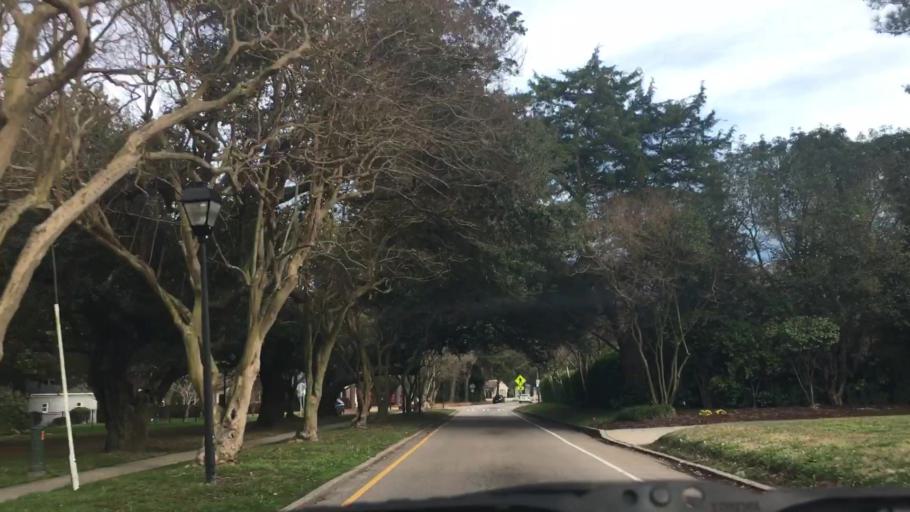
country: US
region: Virginia
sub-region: City of Norfolk
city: Norfolk
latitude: 36.8889
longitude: -76.2726
